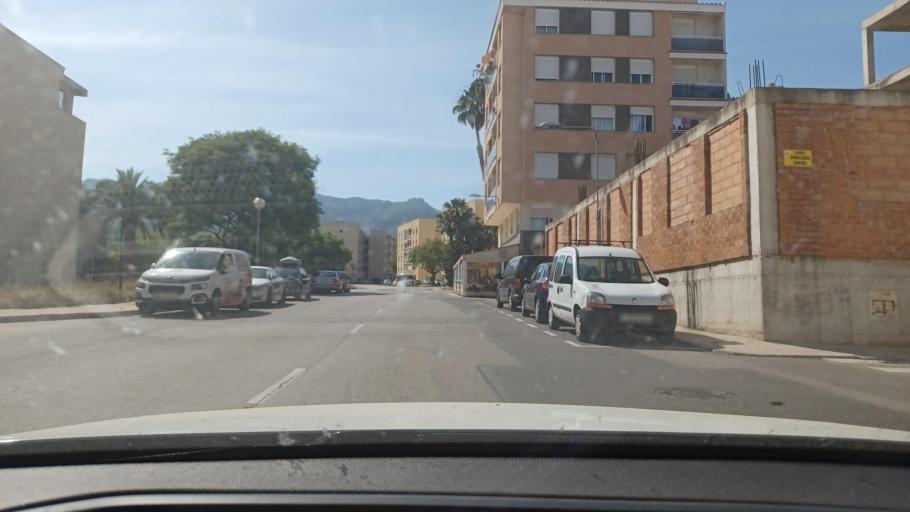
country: ES
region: Catalonia
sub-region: Provincia de Tarragona
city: Sant Carles de la Rapita
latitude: 40.6144
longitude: 0.5843
